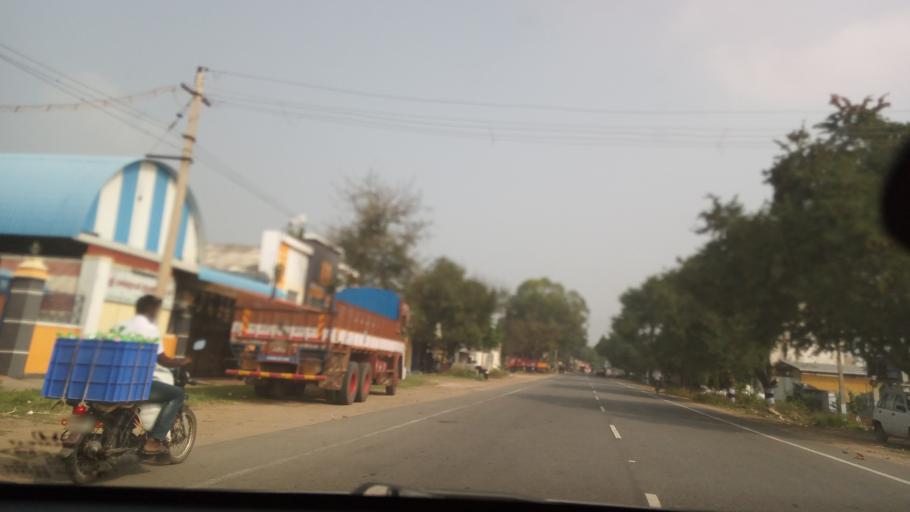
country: IN
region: Tamil Nadu
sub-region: Erode
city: Punjai Puliyampatti
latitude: 11.3594
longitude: 77.1697
